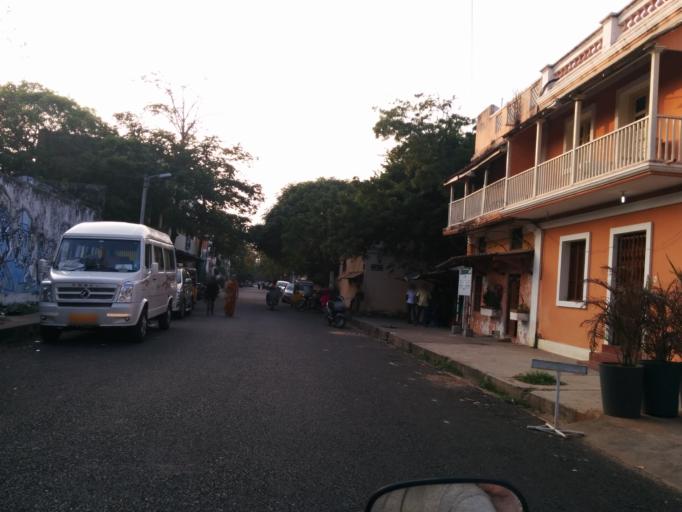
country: IN
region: Pondicherry
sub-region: Puducherry
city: Puducherry
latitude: 11.9275
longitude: 79.8337
